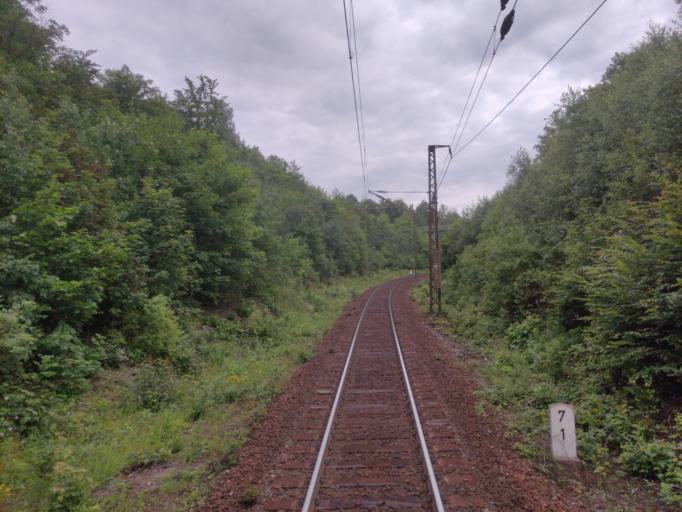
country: DE
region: Saxony-Anhalt
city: Huttenrode
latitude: 51.7863
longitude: 10.9238
